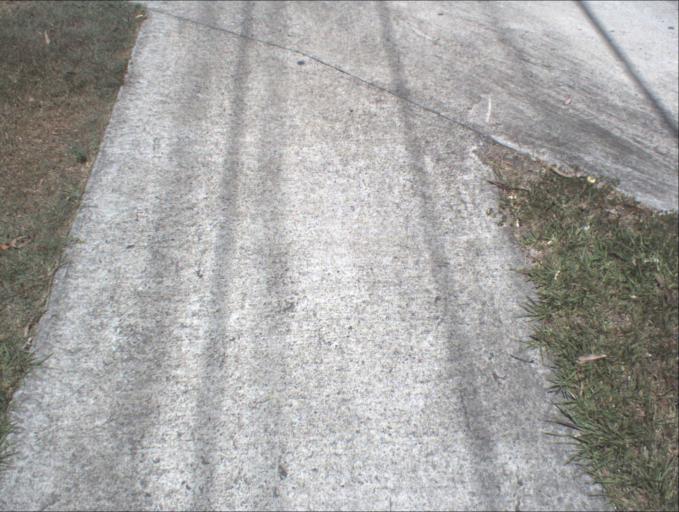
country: AU
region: Queensland
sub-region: Logan
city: Slacks Creek
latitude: -27.6669
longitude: 153.1760
